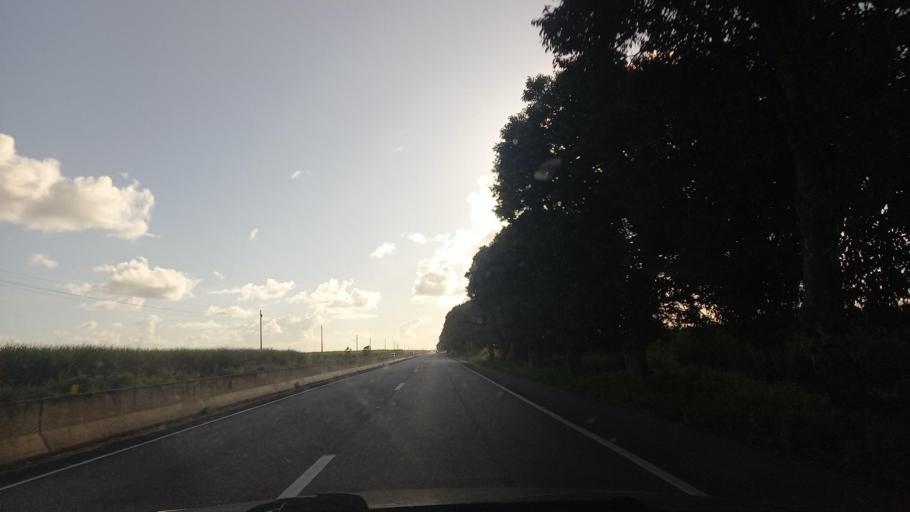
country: BR
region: Alagoas
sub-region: Sao Miguel Dos Campos
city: Sao Miguel dos Campos
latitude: -9.8031
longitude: -36.1413
